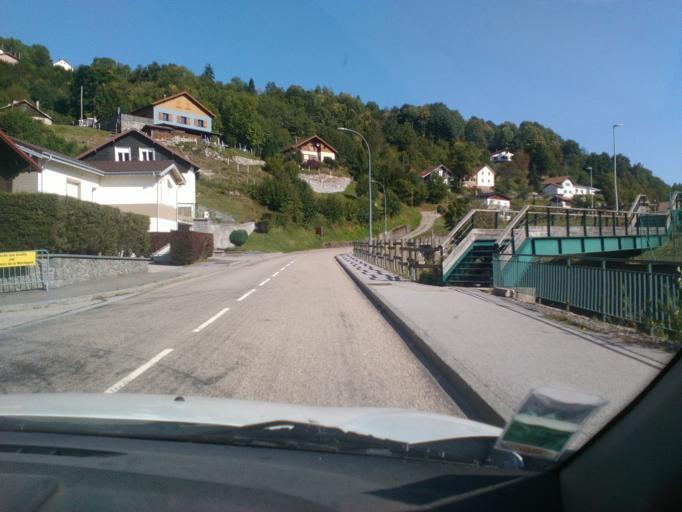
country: FR
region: Lorraine
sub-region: Departement des Vosges
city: La Bresse
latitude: 48.0090
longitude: 6.8827
